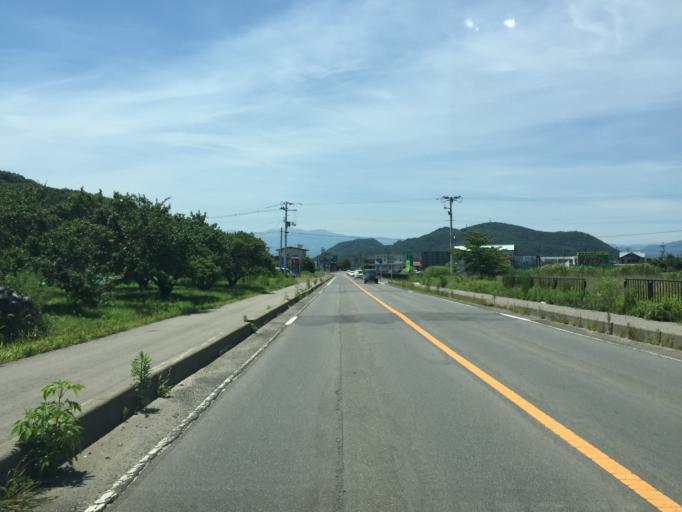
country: JP
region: Fukushima
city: Fukushima-shi
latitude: 37.7719
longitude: 140.5042
